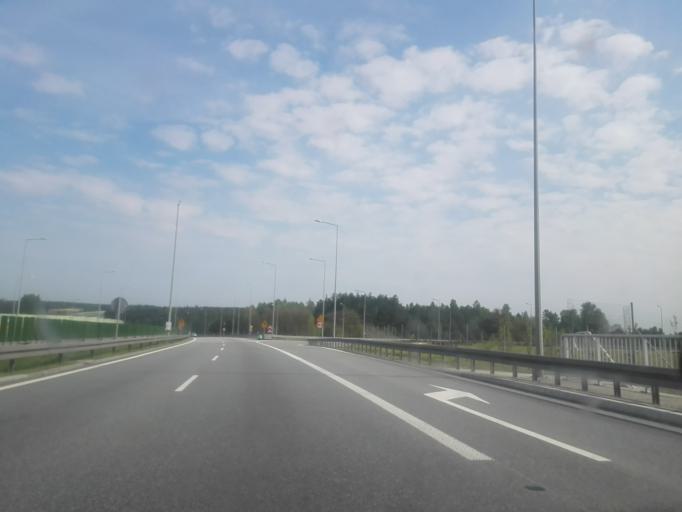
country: PL
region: Lodz Voivodeship
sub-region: Powiat rawski
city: Rawa Mazowiecka
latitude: 51.7037
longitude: 20.2202
